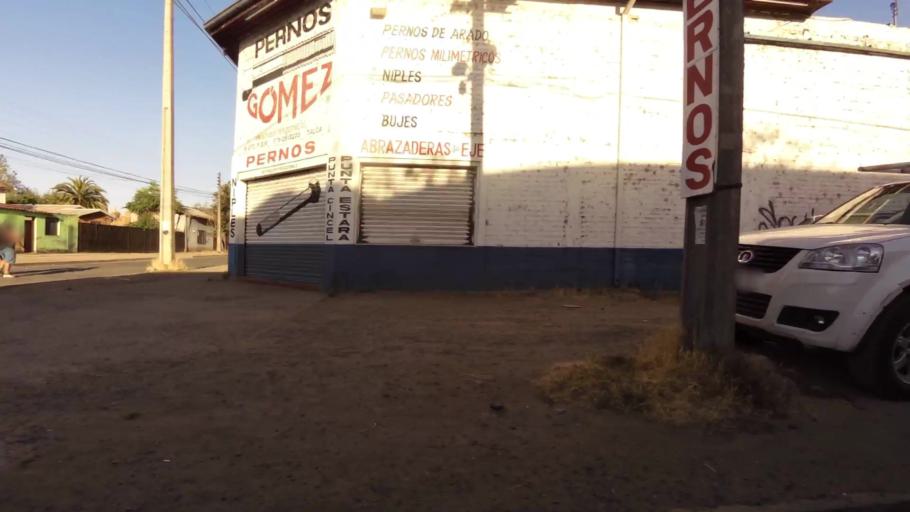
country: CL
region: Maule
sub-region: Provincia de Talca
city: Talca
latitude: -35.4360
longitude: -71.6449
